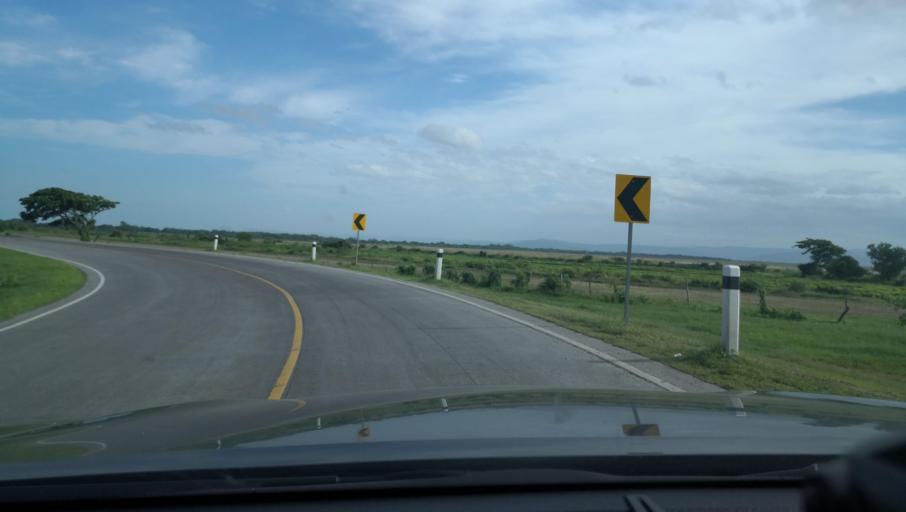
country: NI
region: Masaya
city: Tisma
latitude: 12.1531
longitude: -85.8409
